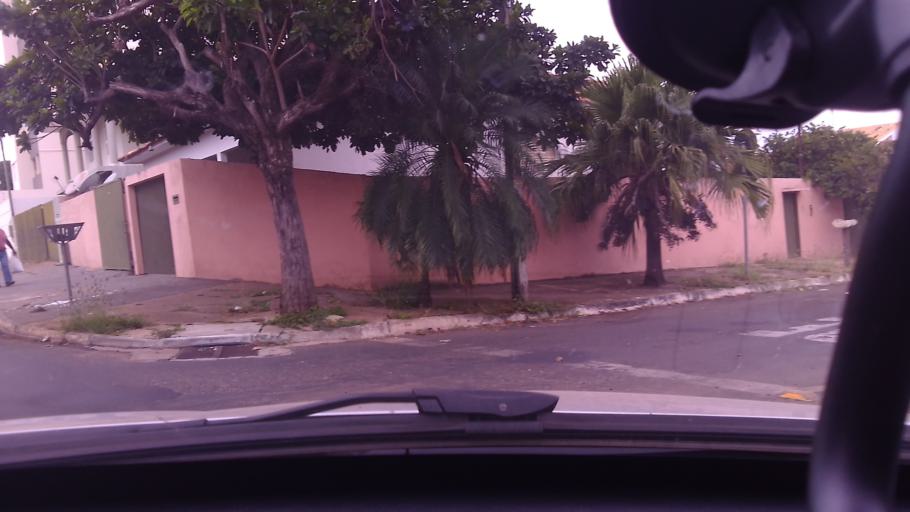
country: BR
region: Goias
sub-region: Mineiros
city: Mineiros
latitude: -17.5653
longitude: -52.5642
